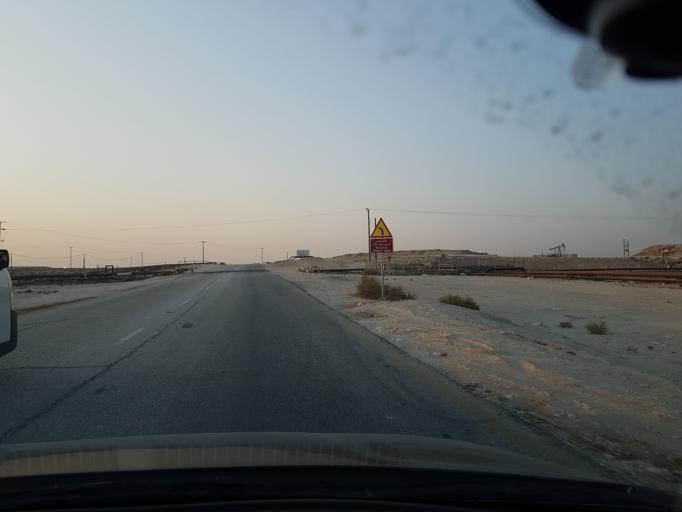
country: BH
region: Central Governorate
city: Dar Kulayb
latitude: 26.0539
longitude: 50.5562
